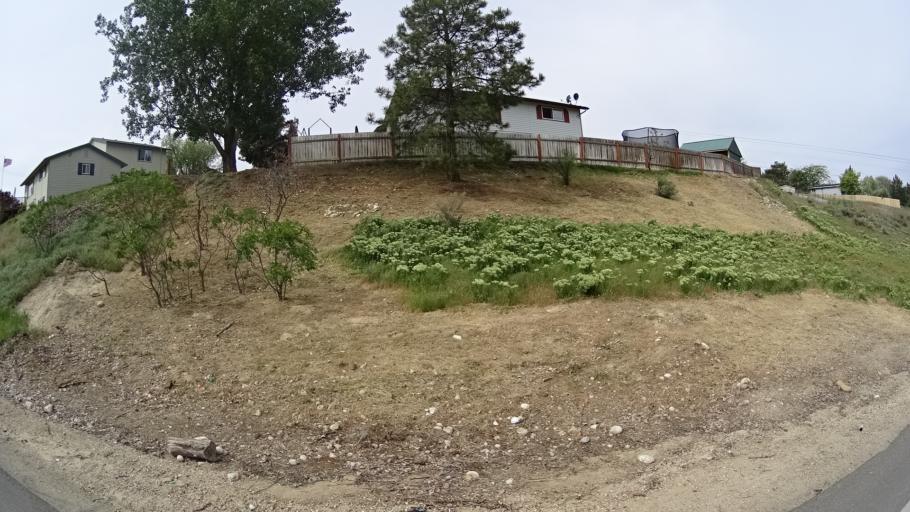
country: US
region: Idaho
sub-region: Ada County
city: Meridian
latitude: 43.5347
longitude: -116.3138
